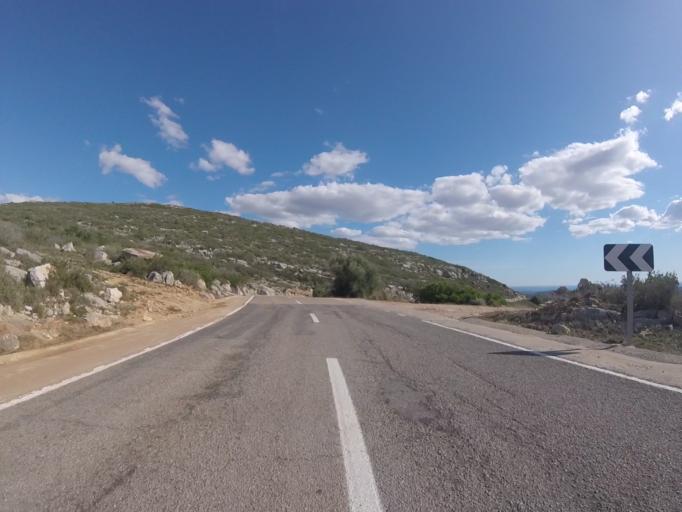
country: ES
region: Valencia
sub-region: Provincia de Castello
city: Alcala de Xivert
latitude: 40.2945
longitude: 0.1802
